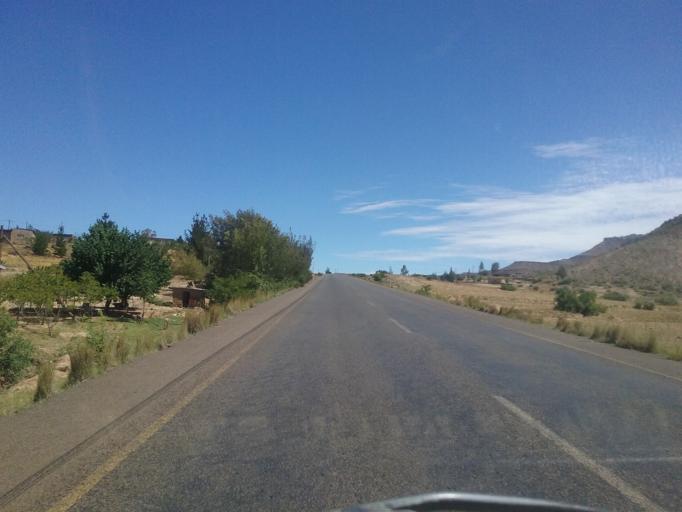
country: LS
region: Quthing
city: Quthing
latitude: -30.3589
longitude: 27.5473
